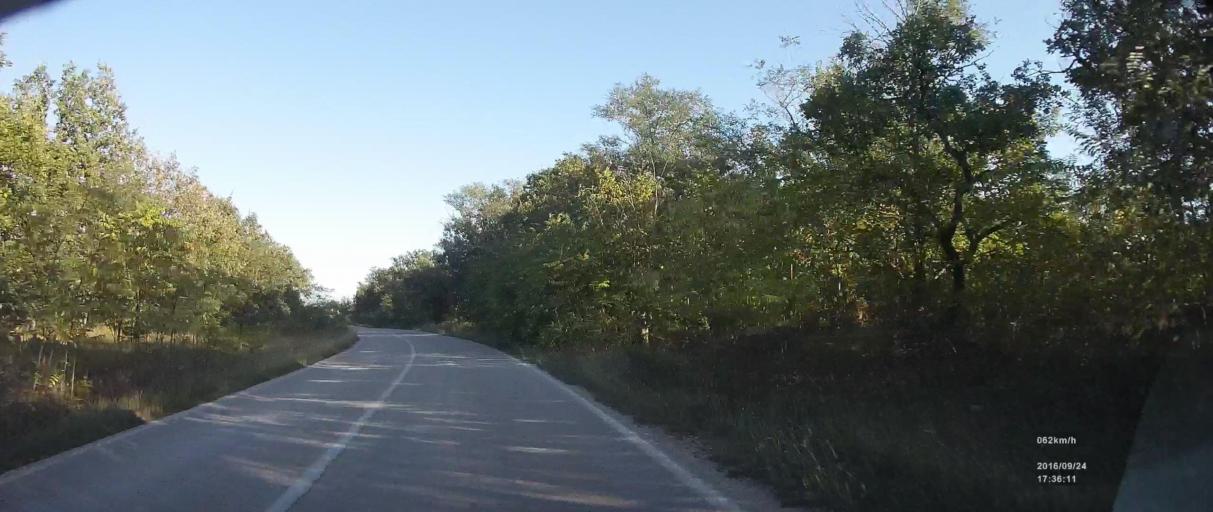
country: HR
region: Zadarska
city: Posedarje
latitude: 44.1563
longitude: 15.4731
